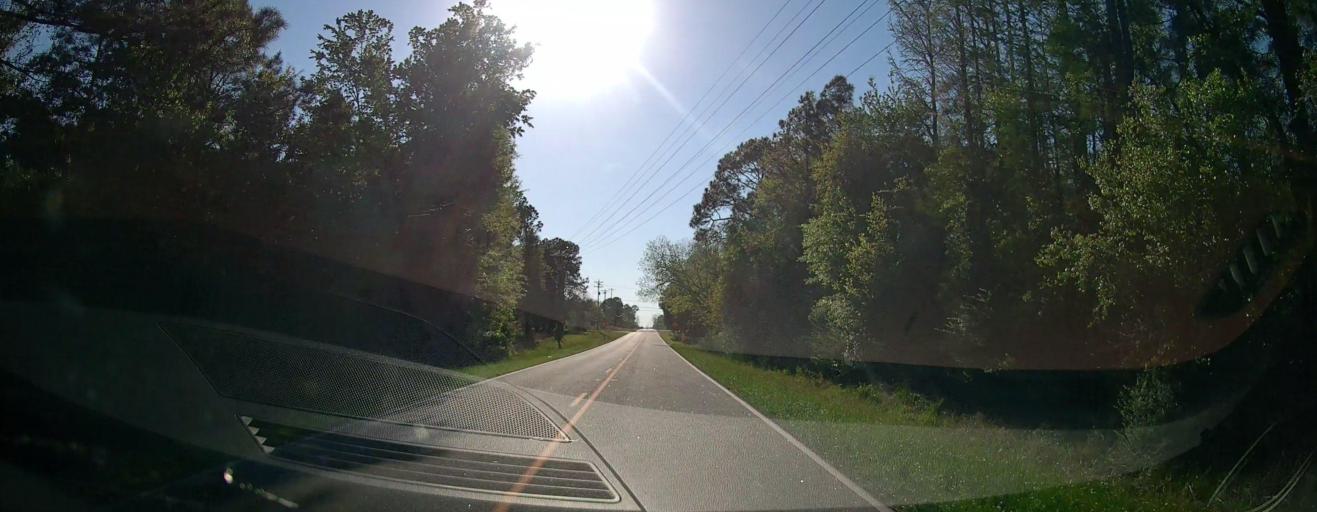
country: US
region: Georgia
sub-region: Ben Hill County
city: Fitzgerald
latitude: 31.7434
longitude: -83.2437
